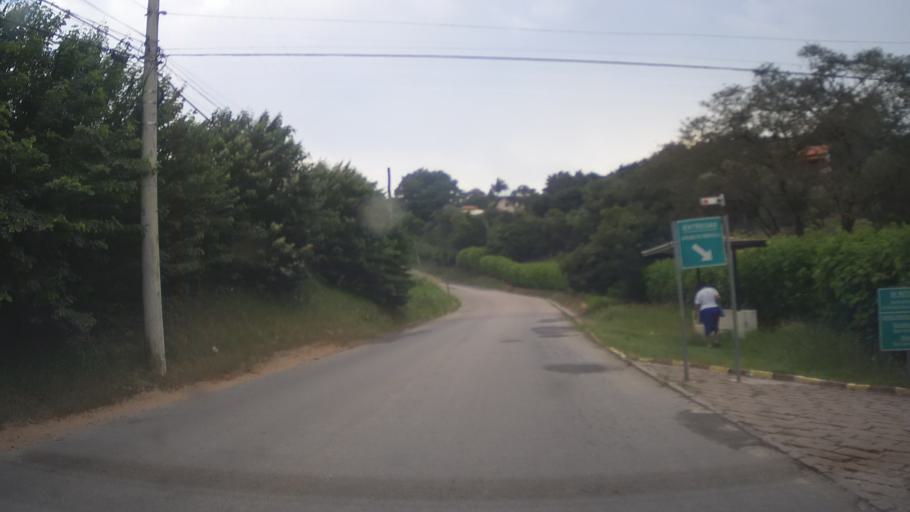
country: BR
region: Sao Paulo
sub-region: Itupeva
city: Itupeva
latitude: -23.1706
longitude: -47.1083
